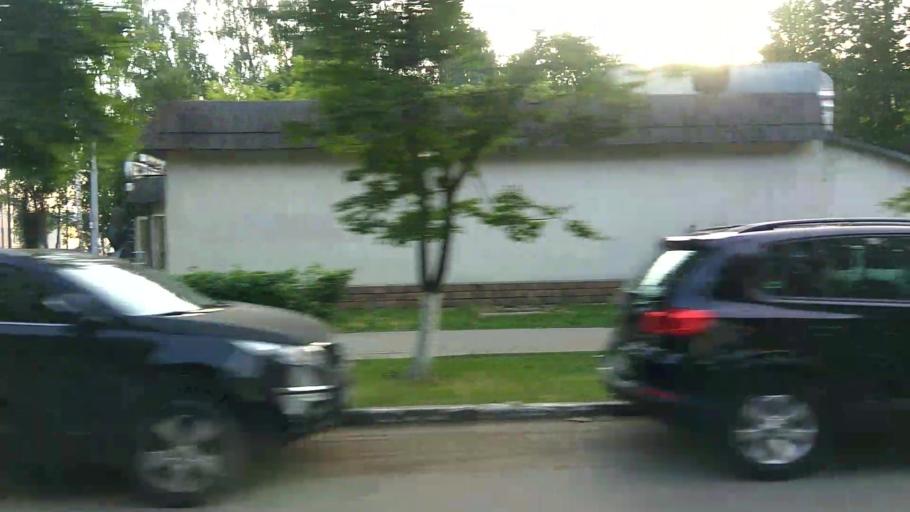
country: RU
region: Moskovskaya
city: Korolev
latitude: 55.9143
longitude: 37.8123
